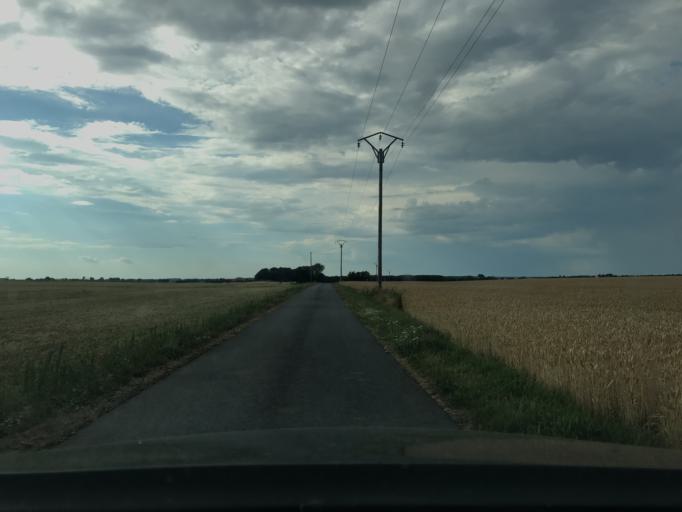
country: SE
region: Skane
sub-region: Simrishamns Kommun
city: Kivik
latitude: 55.5305
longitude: 14.1602
